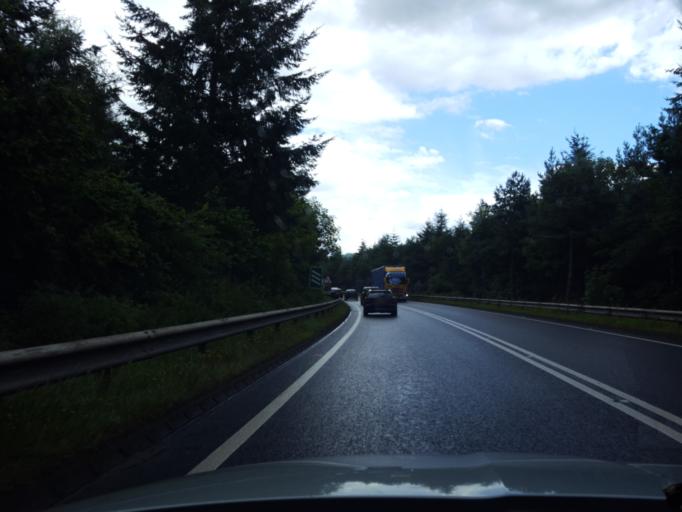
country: GB
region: Scotland
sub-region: Perth and Kinross
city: Pitlochry
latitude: 56.7127
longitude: -3.7624
